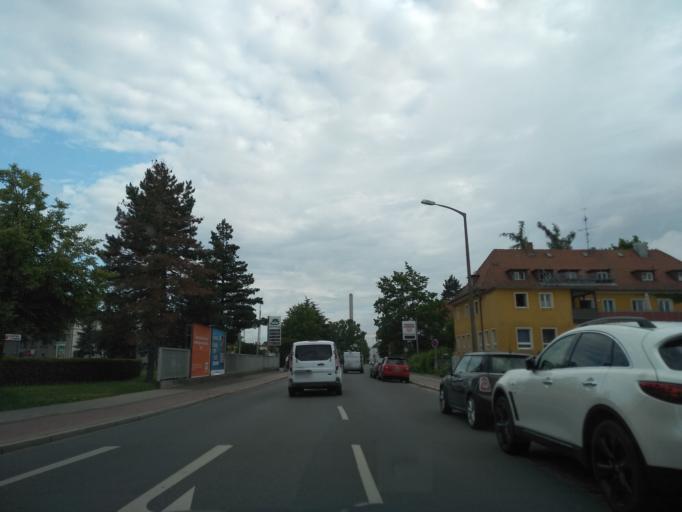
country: DE
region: Bavaria
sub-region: Regierungsbezirk Mittelfranken
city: Erlangen
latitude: 49.5833
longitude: 11.0057
